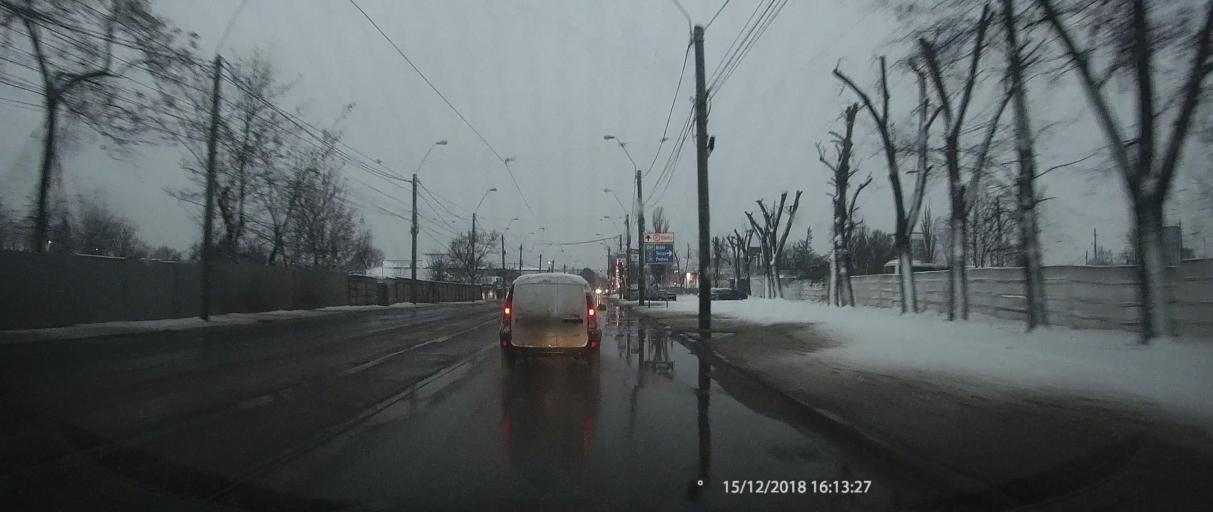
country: RO
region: Galati
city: Galati
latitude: 45.4633
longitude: 28.0336
